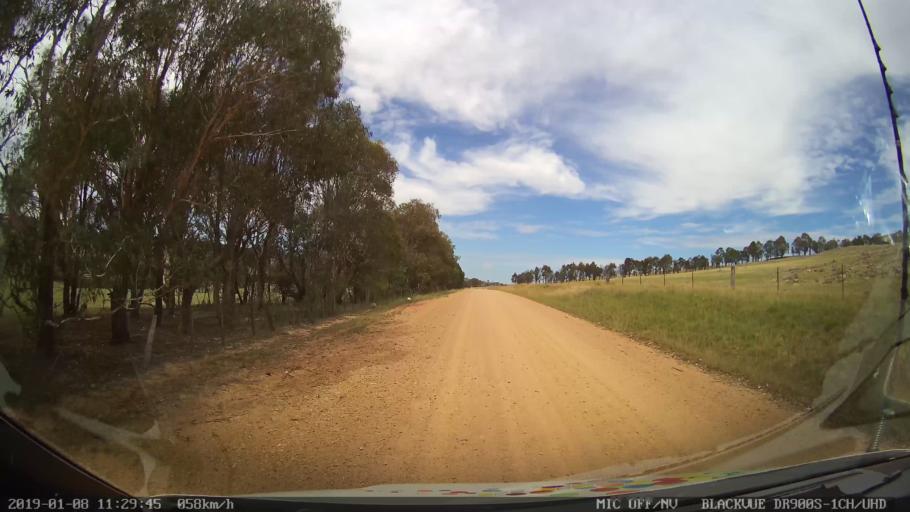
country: AU
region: New South Wales
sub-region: Guyra
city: Guyra
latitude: -30.3027
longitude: 151.5474
